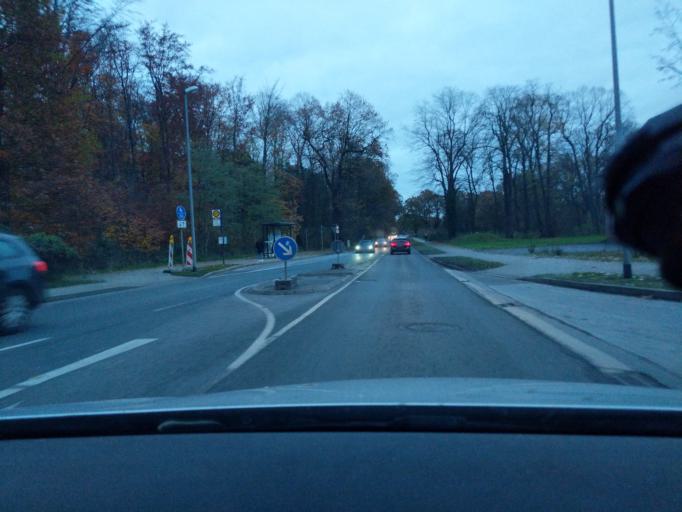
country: DE
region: North Rhine-Westphalia
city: Lunen
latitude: 51.6117
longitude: 7.4787
